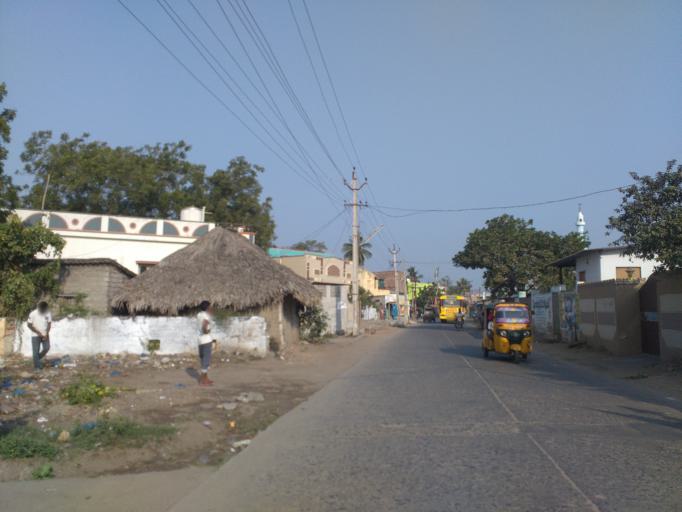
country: IN
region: Andhra Pradesh
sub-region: Prakasam
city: Chirala
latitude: 15.8359
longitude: 80.3630
